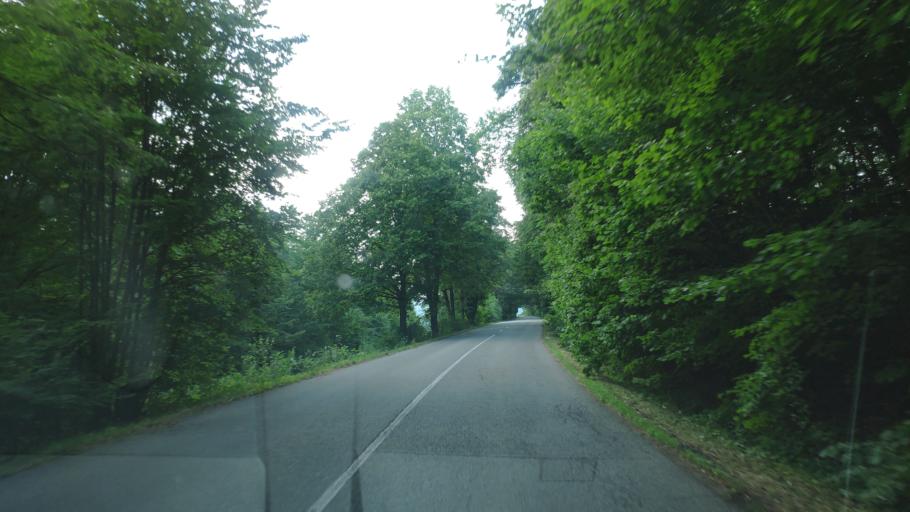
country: SK
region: Kosicky
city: Moldava nad Bodvou
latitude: 48.6908
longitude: 20.9739
